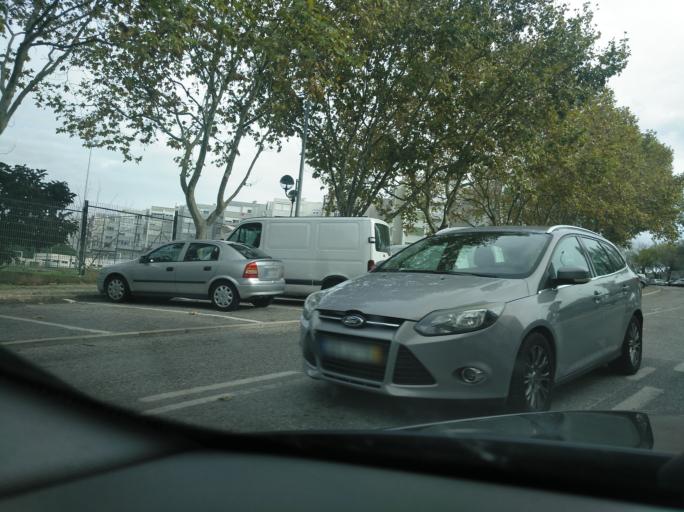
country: PT
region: Lisbon
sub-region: Amadora
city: Amadora
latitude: 38.7418
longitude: -9.2205
